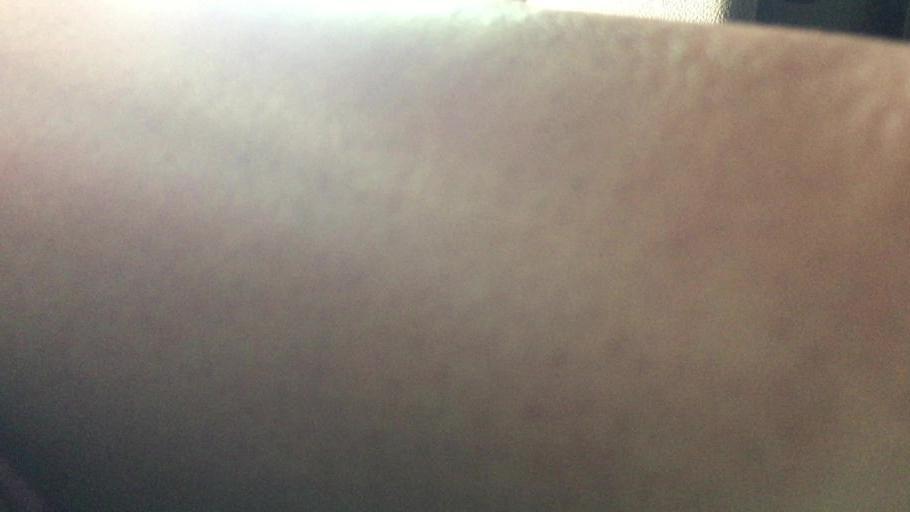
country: US
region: Georgia
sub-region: Carroll County
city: Carrollton
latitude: 33.5970
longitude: -85.0355
